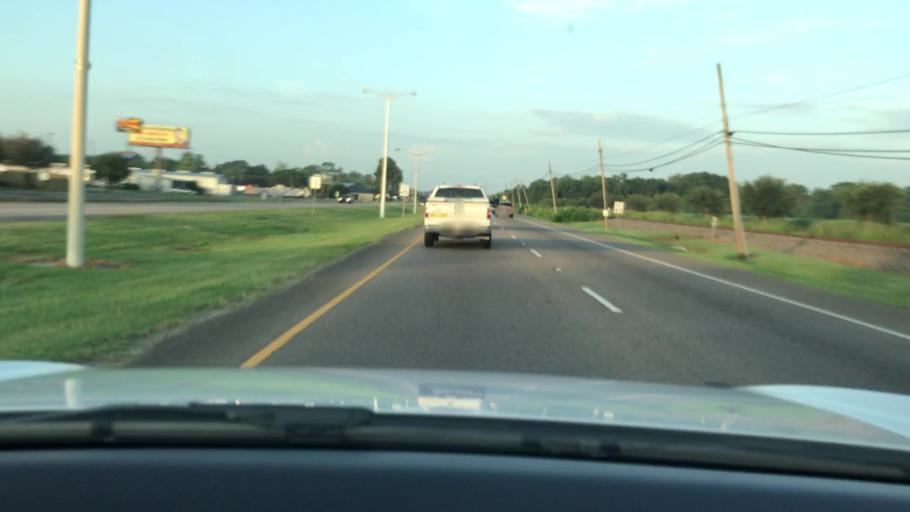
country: US
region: Louisiana
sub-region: West Baton Rouge Parish
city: Brusly
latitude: 30.3856
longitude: -91.2458
